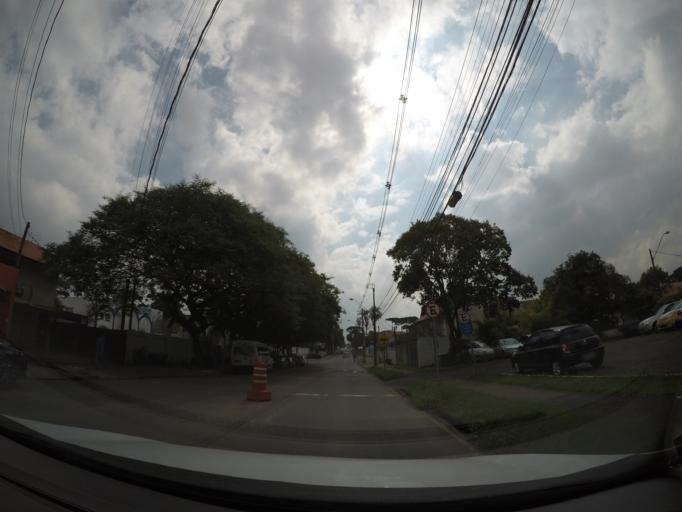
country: BR
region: Parana
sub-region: Sao Jose Dos Pinhais
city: Sao Jose dos Pinhais
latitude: -25.5045
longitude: -49.2485
